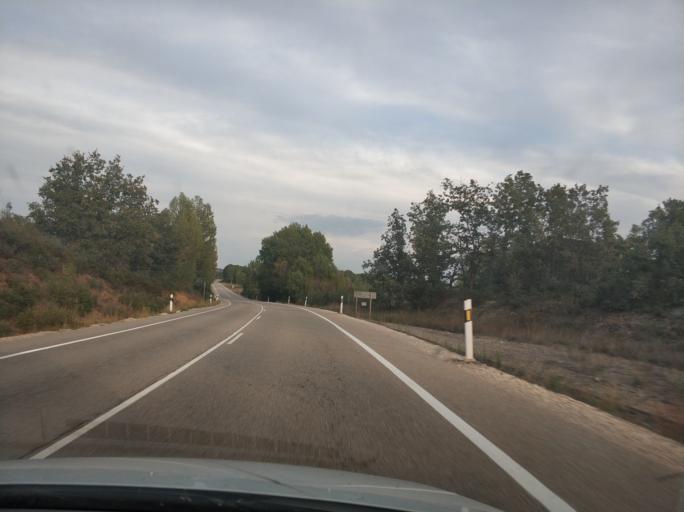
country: ES
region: Castille and Leon
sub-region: Provincia de Burgos
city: Barbadillo del Mercado
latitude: 42.0508
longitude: -3.3775
